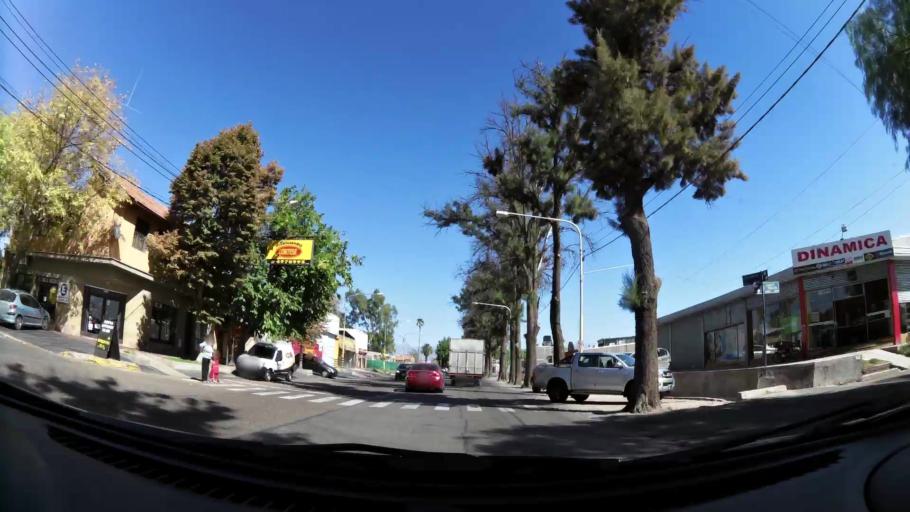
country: AR
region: Mendoza
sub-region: Departamento de Maipu
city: Maipu
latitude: -32.9499
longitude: -68.7892
